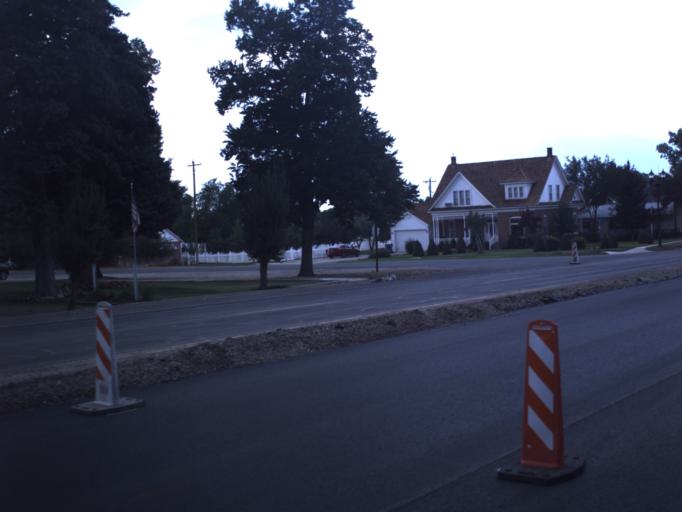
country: US
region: Utah
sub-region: Millard County
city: Fillmore
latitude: 38.9641
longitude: -112.3236
